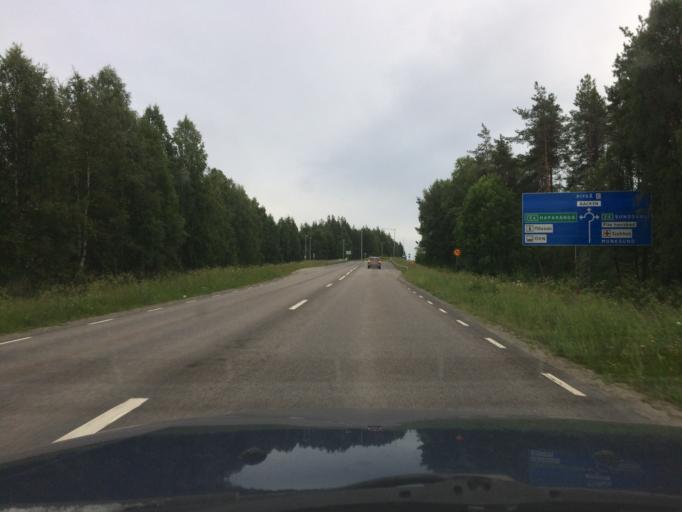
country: SE
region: Norrbotten
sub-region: Pitea Kommun
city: Bergsviken
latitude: 65.3319
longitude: 21.4218
